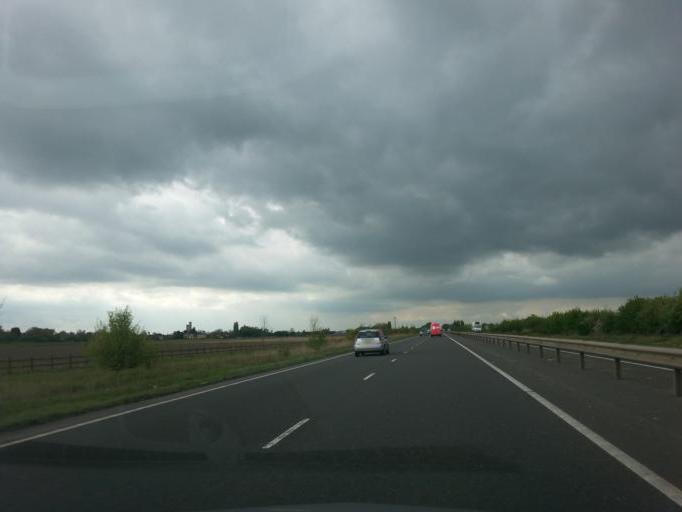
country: GB
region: England
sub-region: Peterborough
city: Thorney
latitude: 52.6253
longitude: -0.0926
